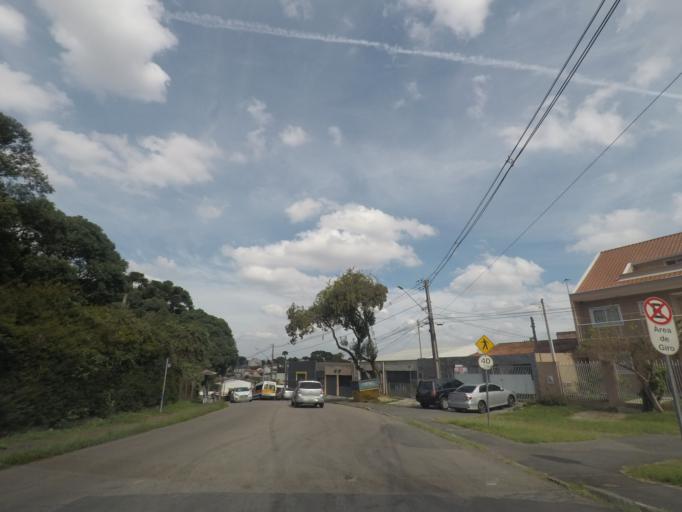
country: BR
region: Parana
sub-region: Curitiba
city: Curitiba
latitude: -25.4896
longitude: -49.2631
